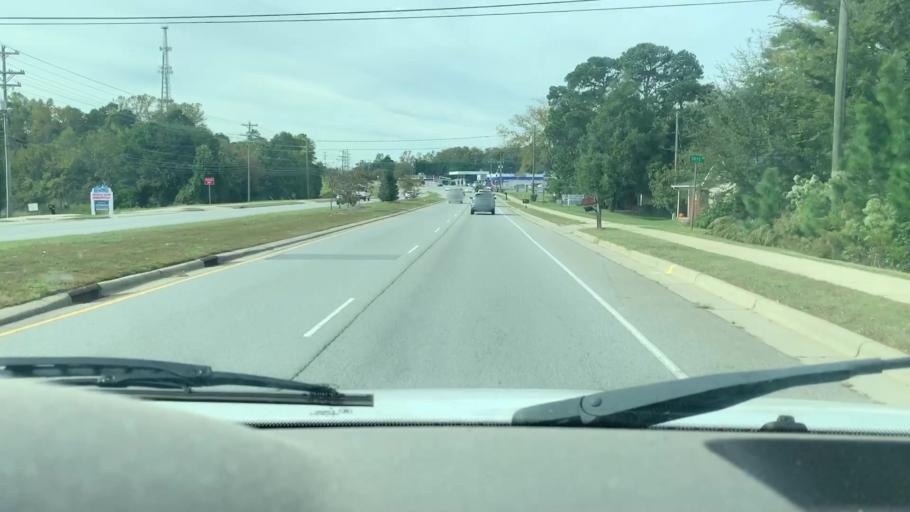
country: US
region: North Carolina
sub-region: Iredell County
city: Mooresville
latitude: 35.5803
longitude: -80.8825
